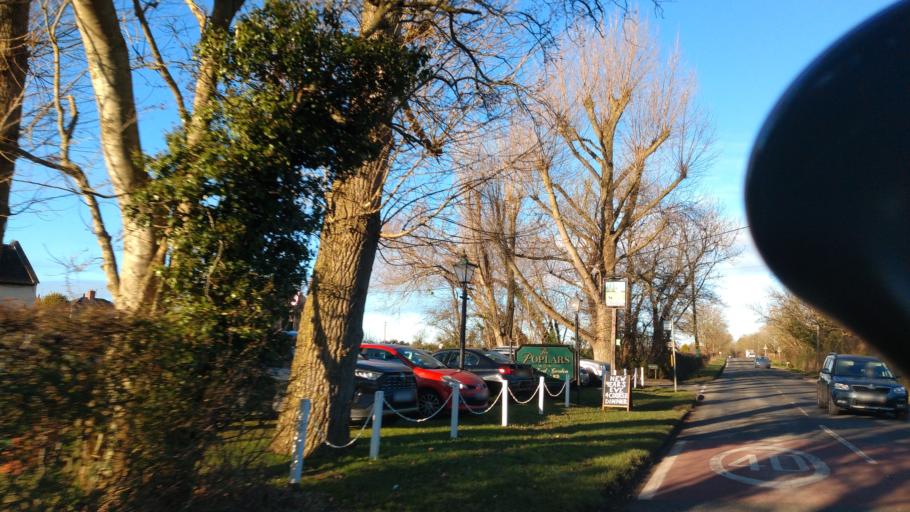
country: GB
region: England
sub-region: Wiltshire
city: Wingfield
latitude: 51.3098
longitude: -2.2571
